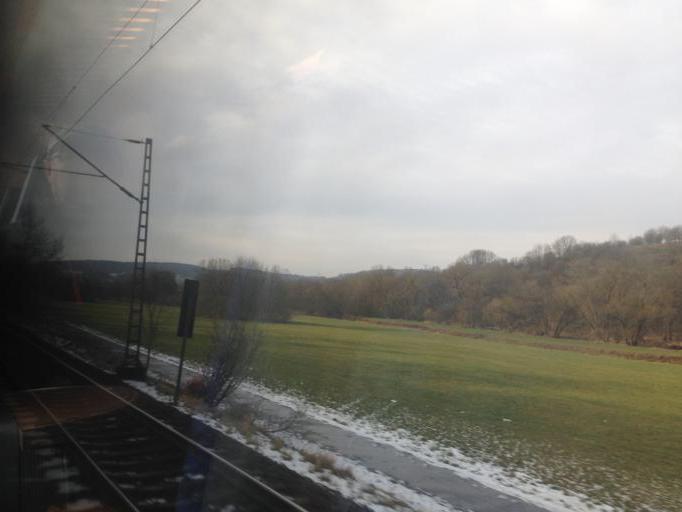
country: DE
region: Hesse
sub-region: Regierungsbezirk Giessen
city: Asslar
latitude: 50.5917
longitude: 8.4382
